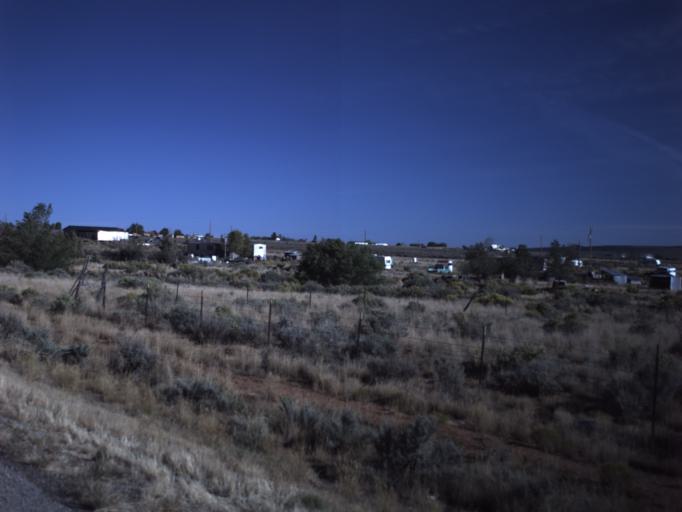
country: US
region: Utah
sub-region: Grand County
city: Moab
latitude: 38.3093
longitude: -109.2928
